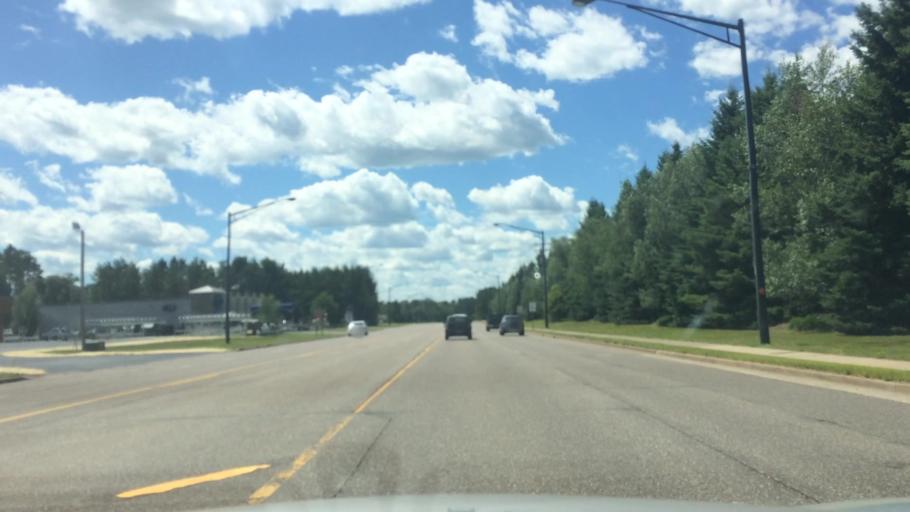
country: US
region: Wisconsin
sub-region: Vilas County
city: Lac du Flambeau
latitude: 45.8854
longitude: -89.7262
